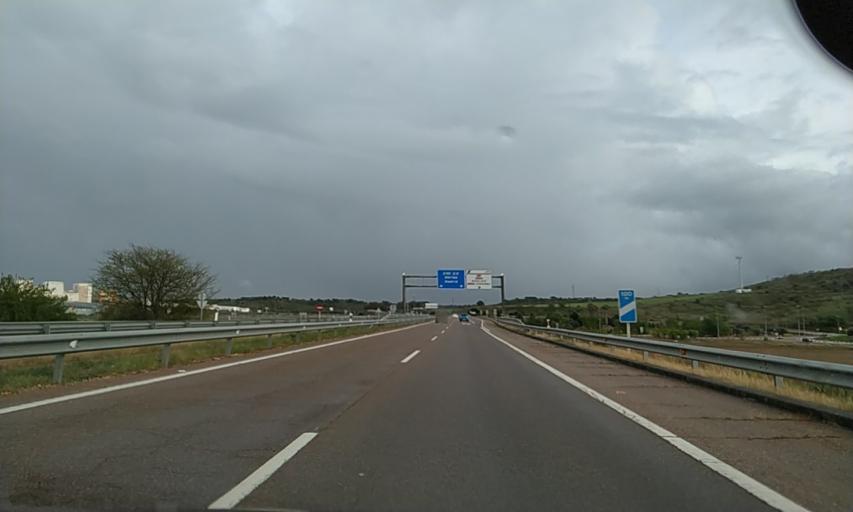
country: ES
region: Extremadura
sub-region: Provincia de Badajoz
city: Badajoz
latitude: 38.8917
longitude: -6.9180
